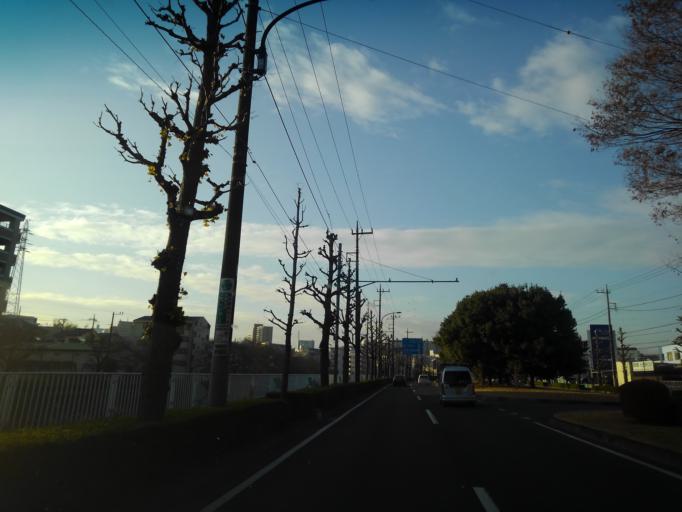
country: JP
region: Tokyo
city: Hino
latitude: 35.6378
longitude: 139.4498
